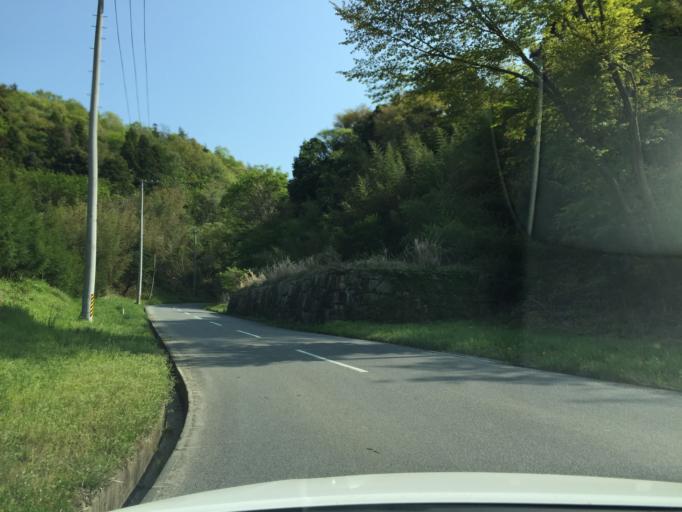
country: JP
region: Fukushima
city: Iwaki
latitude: 37.1363
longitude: 140.8729
